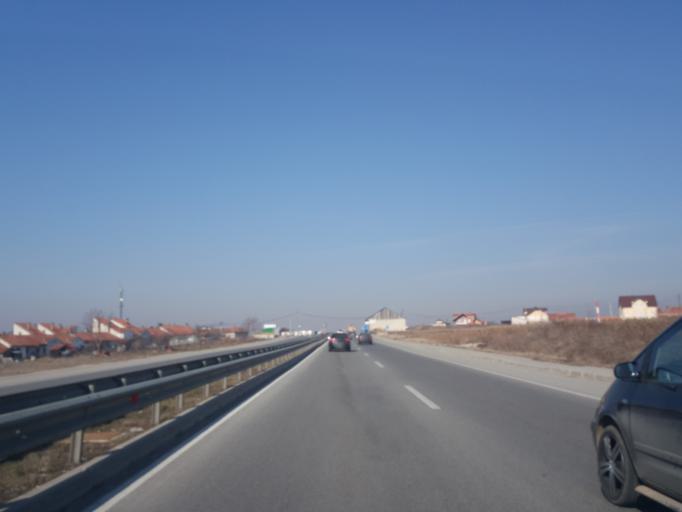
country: XK
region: Pristina
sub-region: Komuna e Obiliqit
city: Obiliq
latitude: 42.7571
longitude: 21.0343
